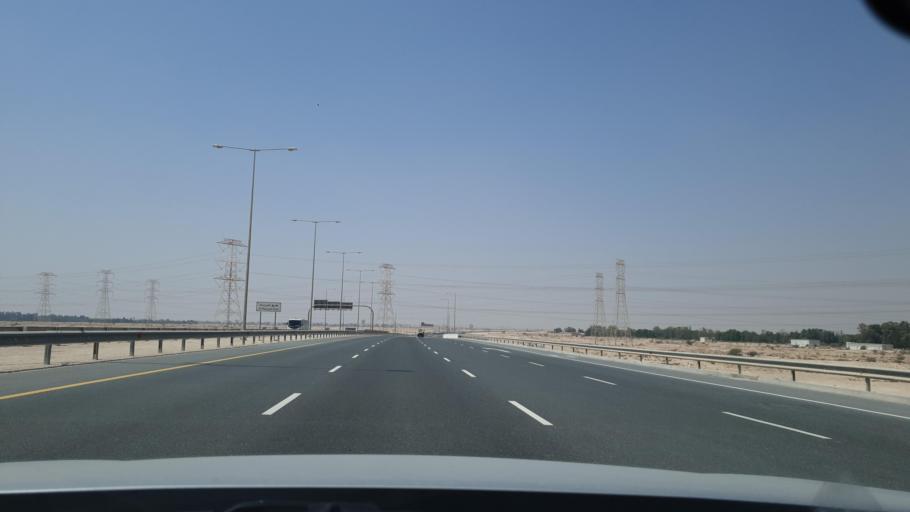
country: QA
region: Baladiyat az Za`ayin
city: Az Za`ayin
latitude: 25.6176
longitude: 51.3608
